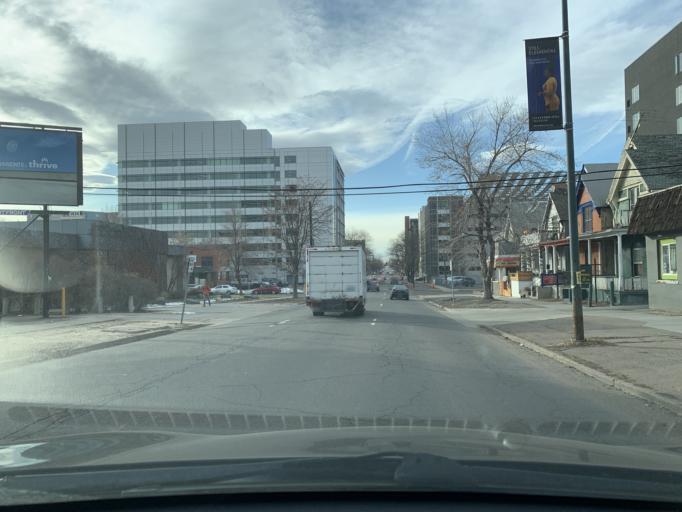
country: US
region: Colorado
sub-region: Denver County
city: Denver
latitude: 39.7369
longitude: -104.9933
